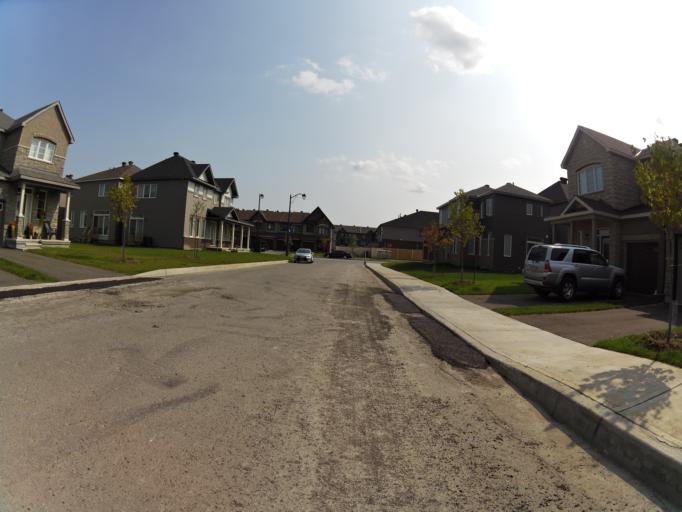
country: CA
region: Ontario
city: Bells Corners
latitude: 45.3056
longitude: -75.9380
